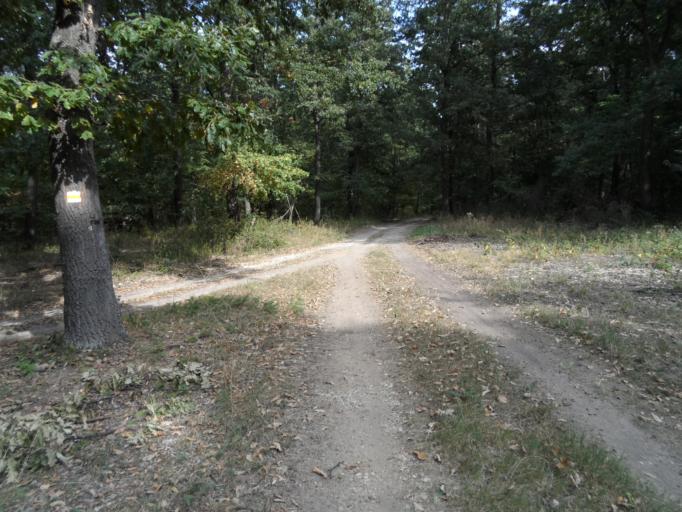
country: HU
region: Veszprem
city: Ajka
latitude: 47.1736
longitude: 17.5142
